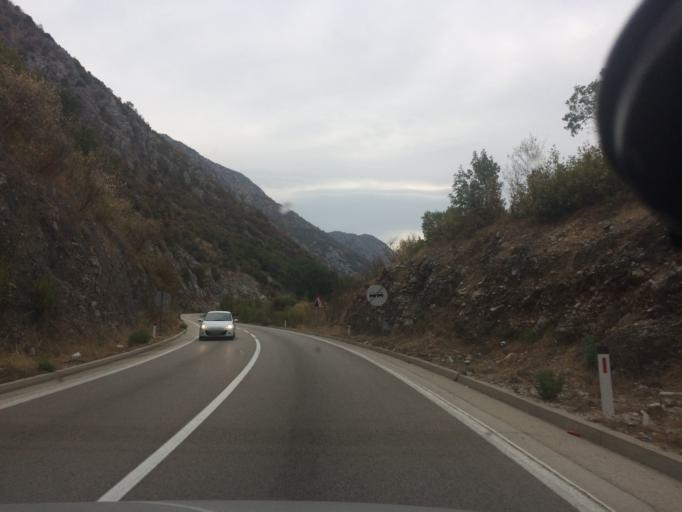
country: ME
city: Lipci
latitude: 42.4920
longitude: 18.6456
